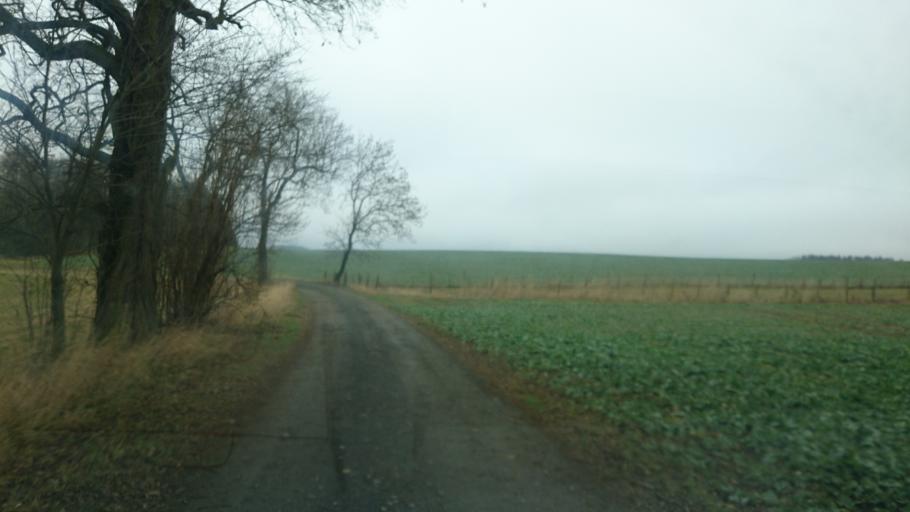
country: DE
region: Thuringia
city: Tanna
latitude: 50.5199
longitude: 11.8672
